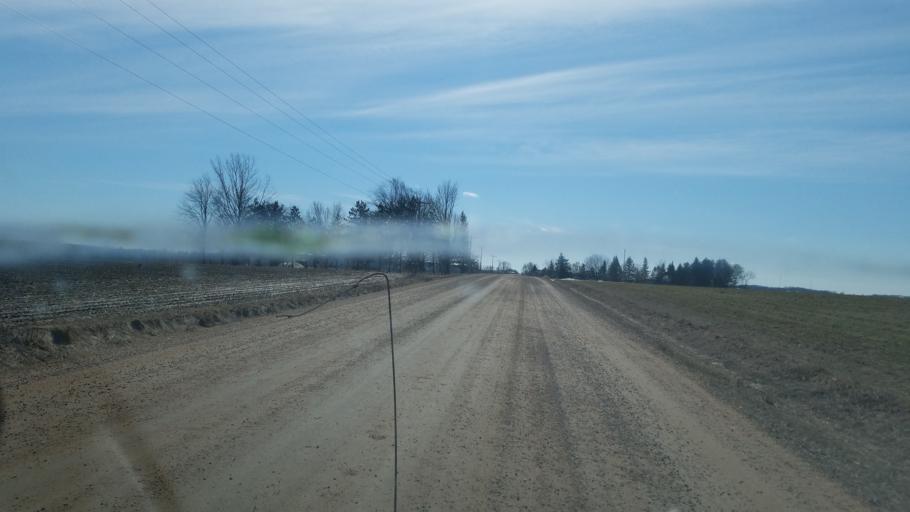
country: US
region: Wisconsin
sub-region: Clark County
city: Loyal
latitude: 44.6067
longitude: -90.4565
